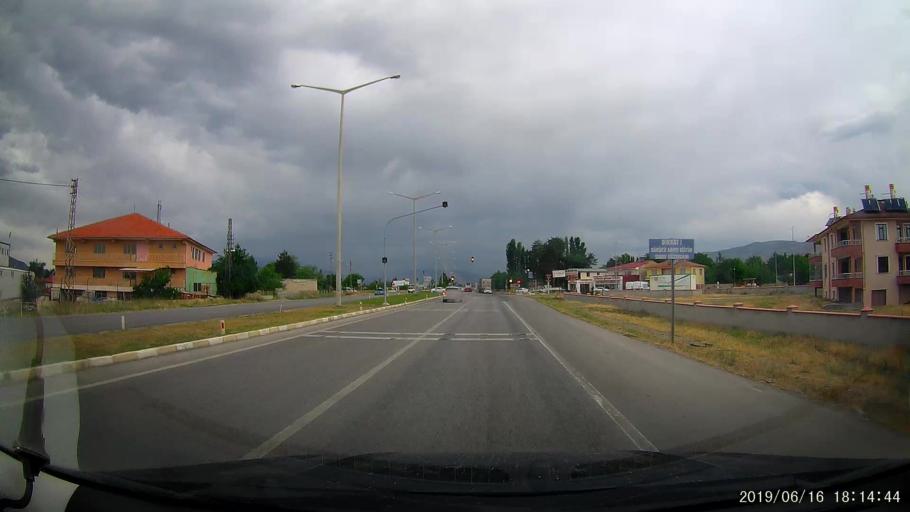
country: TR
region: Erzincan
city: Erzincan
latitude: 39.7259
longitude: 39.5541
